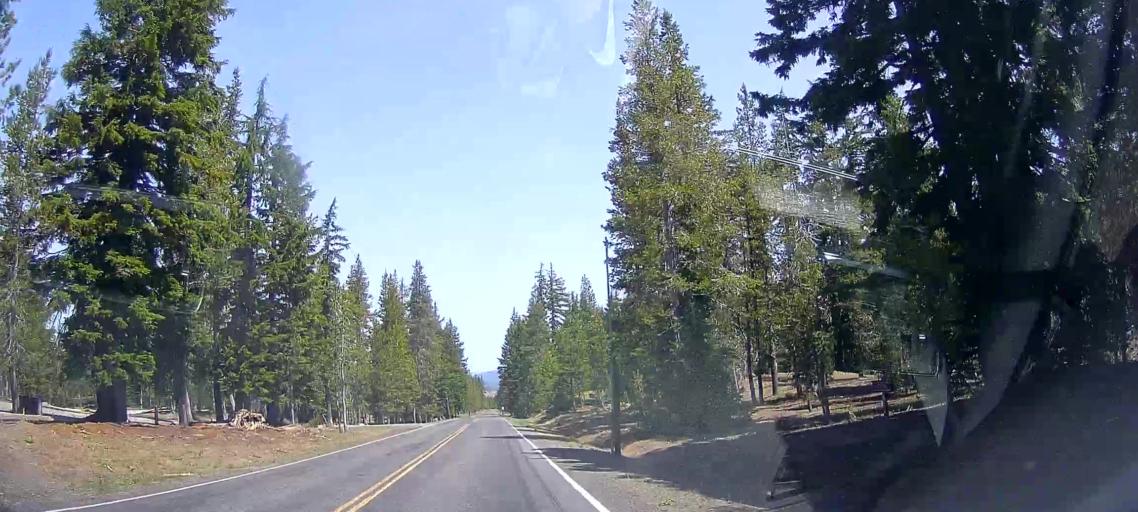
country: US
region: Oregon
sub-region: Jackson County
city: Shady Cove
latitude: 42.9958
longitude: -122.1357
